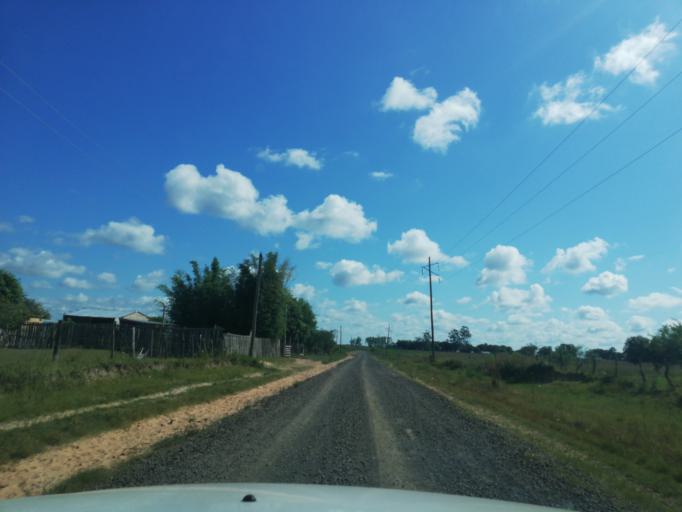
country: AR
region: Corrientes
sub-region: Departamento de San Miguel
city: San Miguel
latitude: -27.9851
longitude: -57.5835
